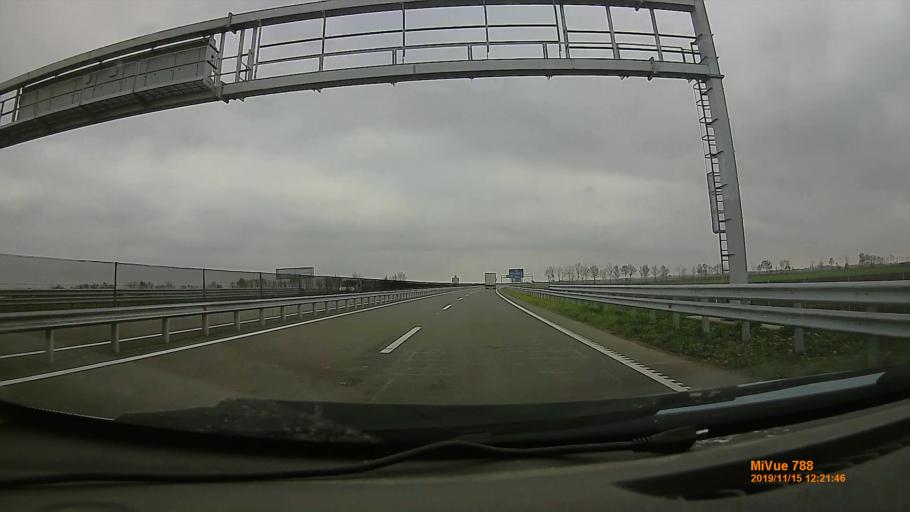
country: HU
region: Bekes
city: Kondoros
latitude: 46.8080
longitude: 20.6875
